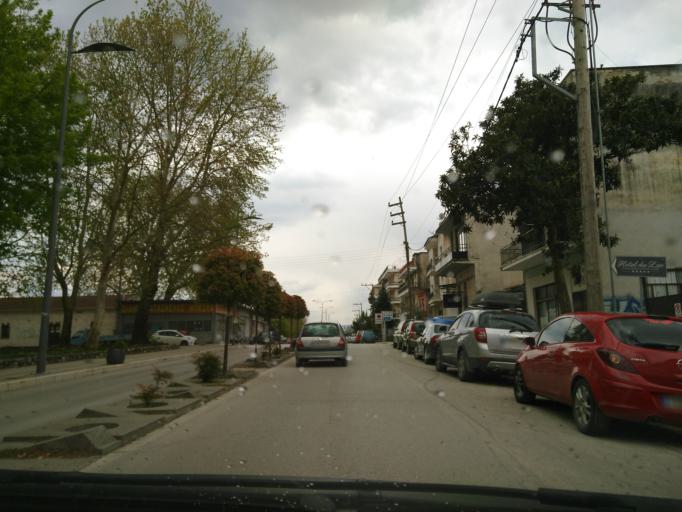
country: GR
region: Epirus
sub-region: Nomos Ioanninon
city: Ioannina
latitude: 39.6658
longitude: 20.8587
